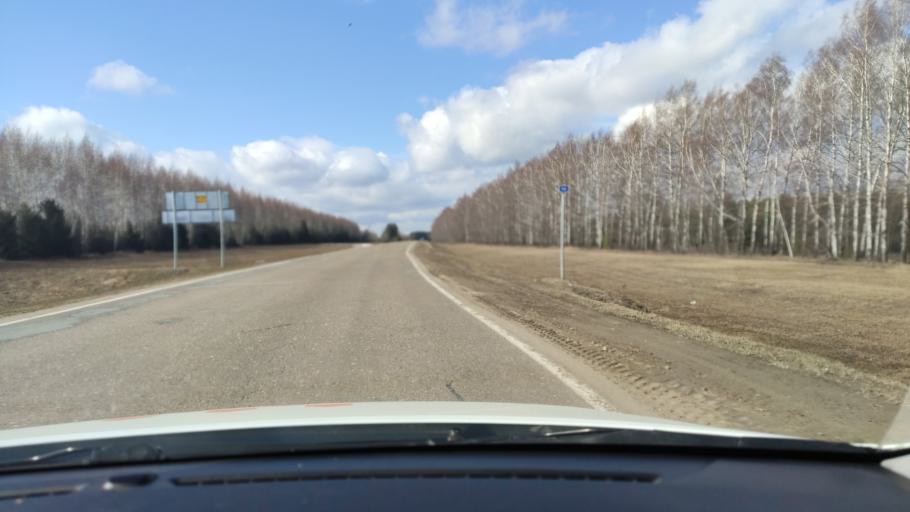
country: RU
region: Tatarstan
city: Vysokaya Gora
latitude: 56.0388
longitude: 49.2269
